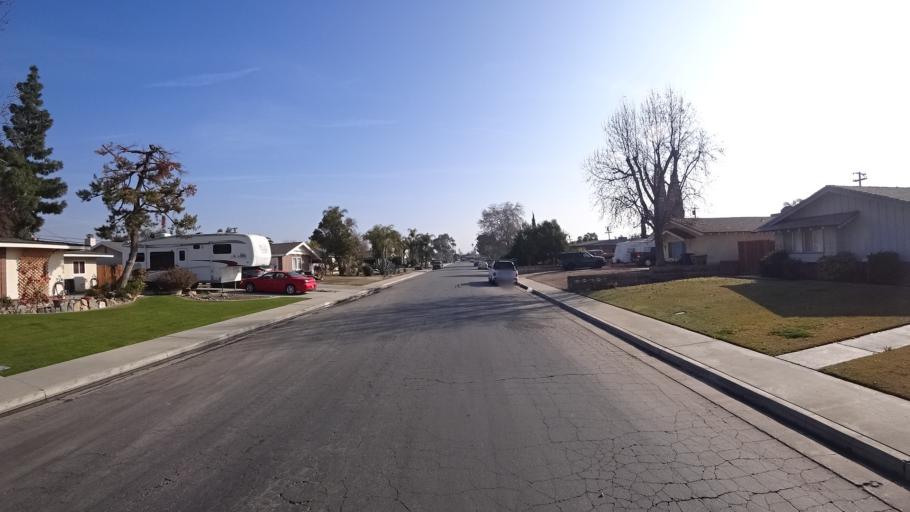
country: US
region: California
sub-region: Kern County
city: Bakersfield
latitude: 35.3273
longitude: -119.0289
